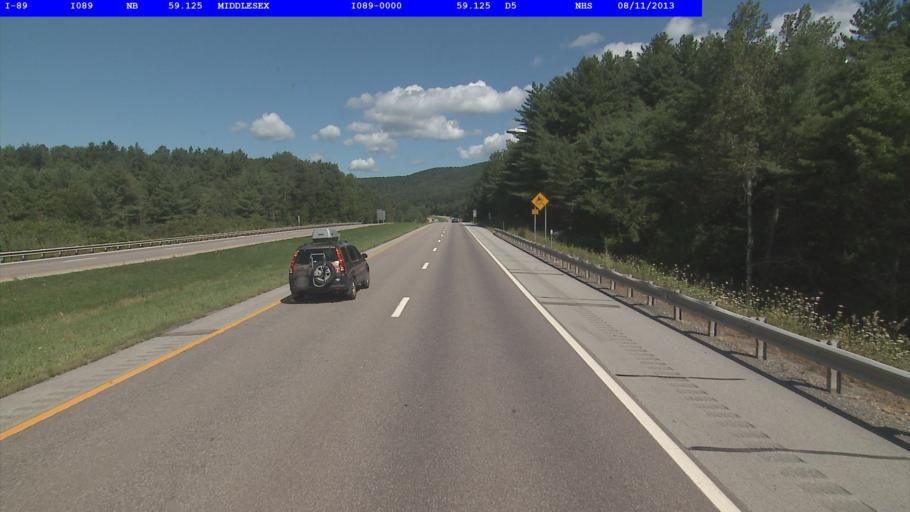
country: US
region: Vermont
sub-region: Washington County
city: Waterbury
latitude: 44.3031
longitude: -72.6893
